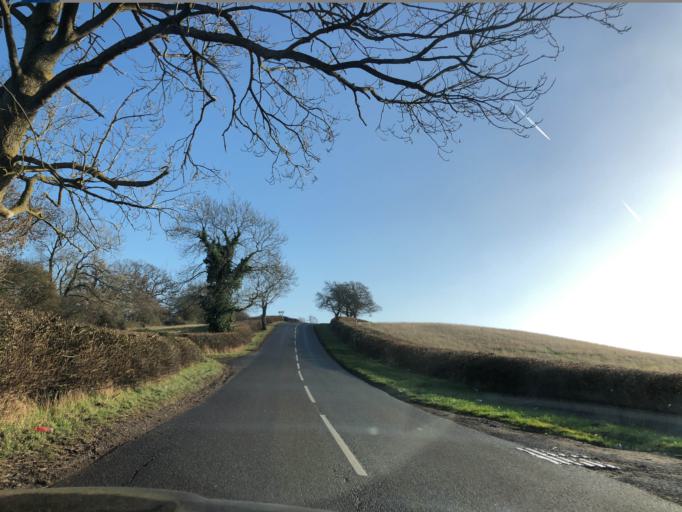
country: GB
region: England
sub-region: Warwickshire
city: Wellesbourne Mountford
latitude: 52.1915
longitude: -1.5718
